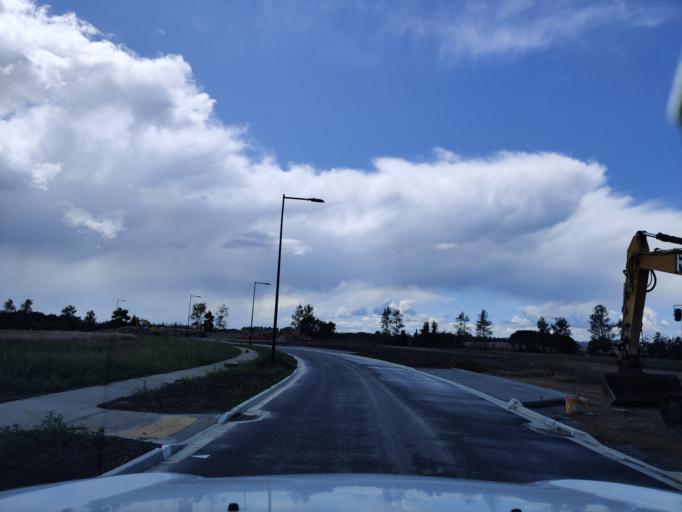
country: NZ
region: Waikato
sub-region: Waikato District
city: Te Kauwhata
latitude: -37.4117
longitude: 175.1524
